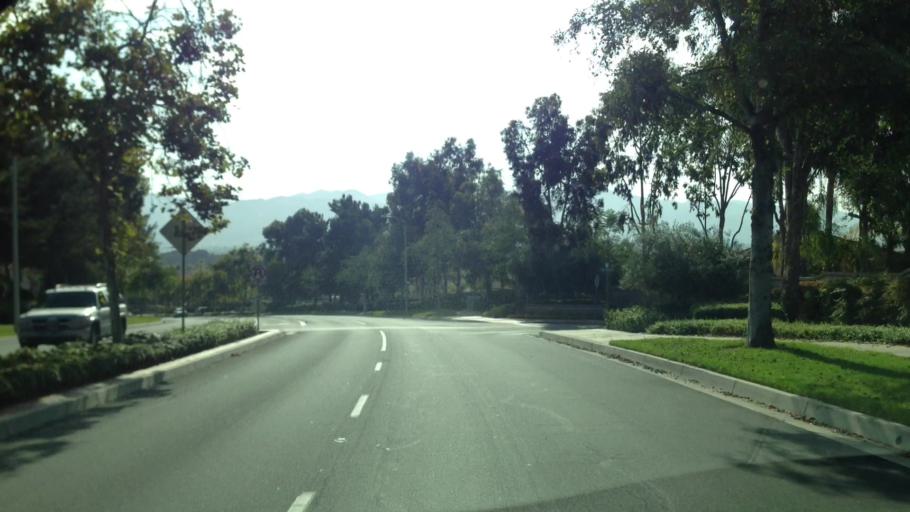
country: US
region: California
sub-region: Orange County
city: Rancho Santa Margarita
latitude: 33.6478
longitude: -117.6167
